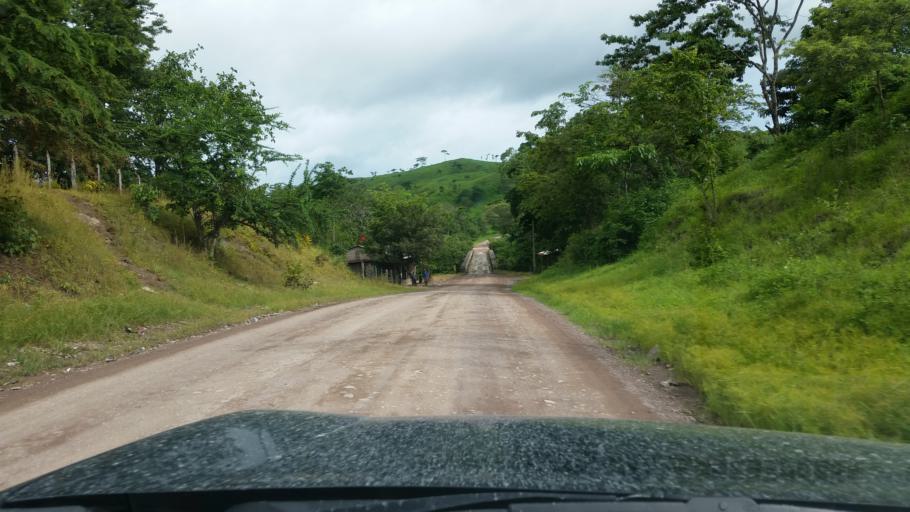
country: NI
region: Atlantico Norte (RAAN)
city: Siuna
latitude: 13.5296
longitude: -84.8232
